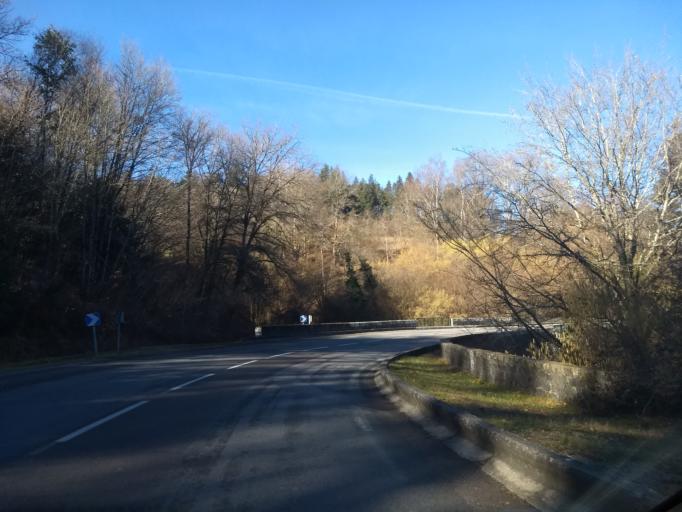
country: FR
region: Limousin
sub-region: Departement de la Haute-Vienne
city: Eymoutiers
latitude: 45.7191
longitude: 1.7608
